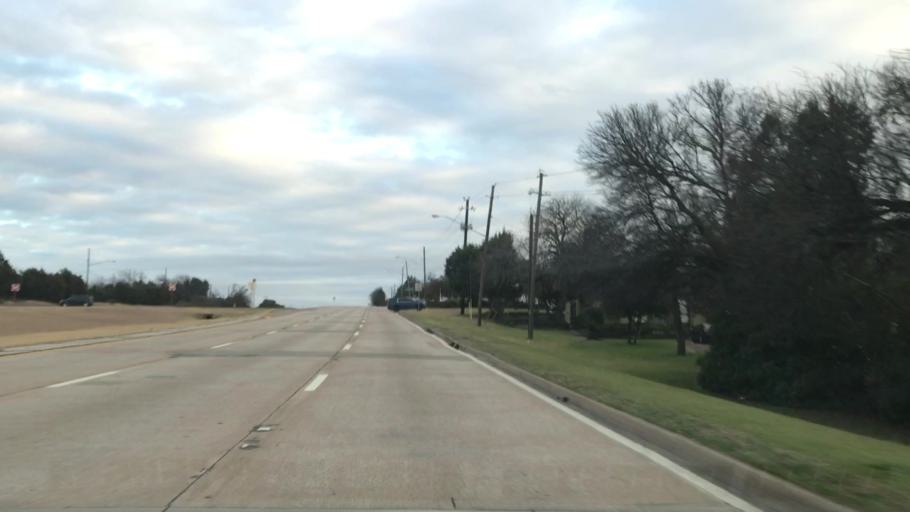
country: US
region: Texas
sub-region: Dallas County
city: Cockrell Hill
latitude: 32.6992
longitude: -96.8983
